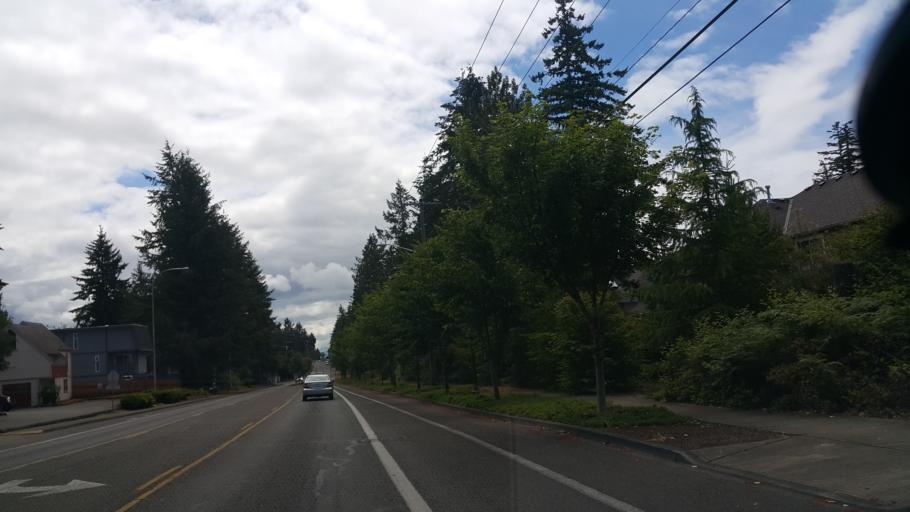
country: US
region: Washington
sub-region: Pierce County
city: Fircrest
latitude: 47.2193
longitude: -122.5265
